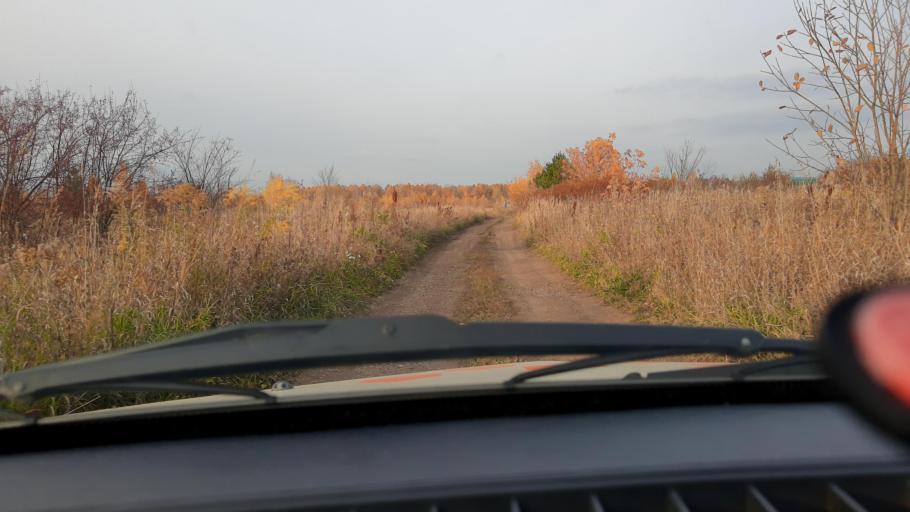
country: RU
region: Bashkortostan
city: Iglino
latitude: 54.8017
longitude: 56.3469
